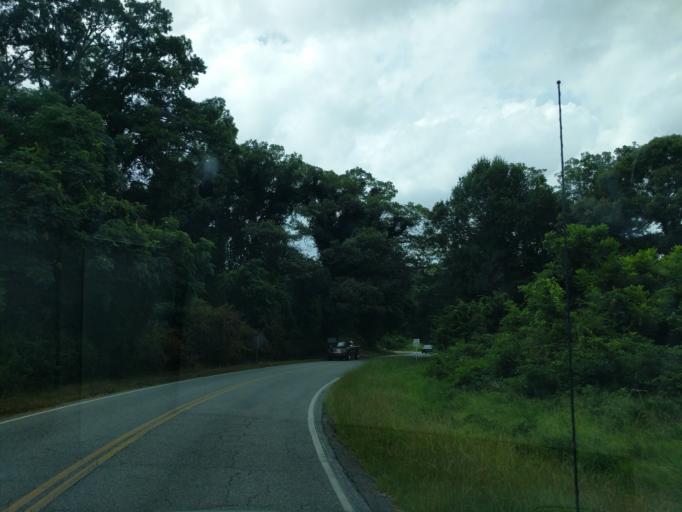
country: US
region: South Carolina
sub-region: Anderson County
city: Anderson
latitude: 34.5043
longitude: -82.6028
